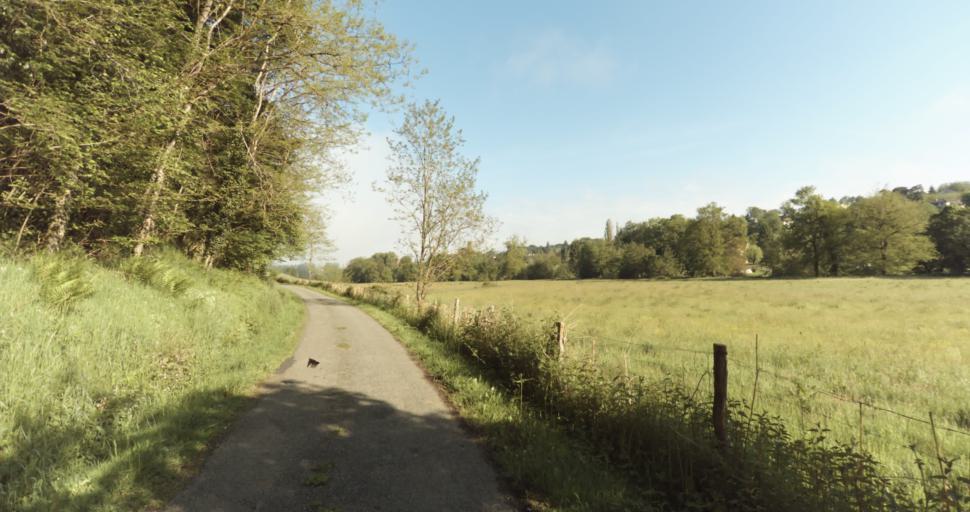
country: FR
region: Limousin
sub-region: Departement de la Haute-Vienne
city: Le Vigen
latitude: 45.7499
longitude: 1.2851
